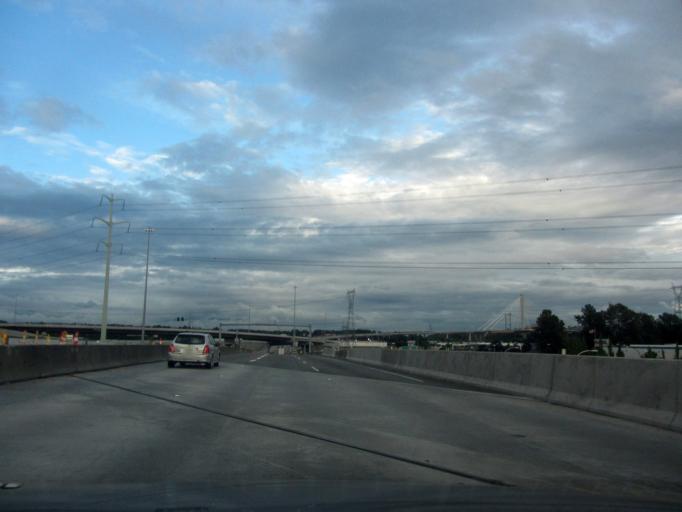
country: CA
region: British Columbia
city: Port Moody
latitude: 49.2293
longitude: -122.8350
